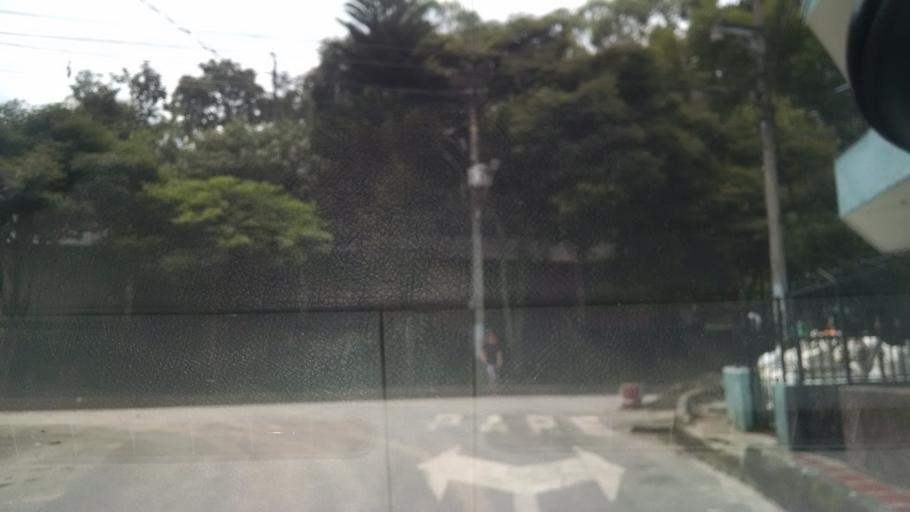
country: CO
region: Antioquia
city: Itagui
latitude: 6.2019
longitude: -75.5902
